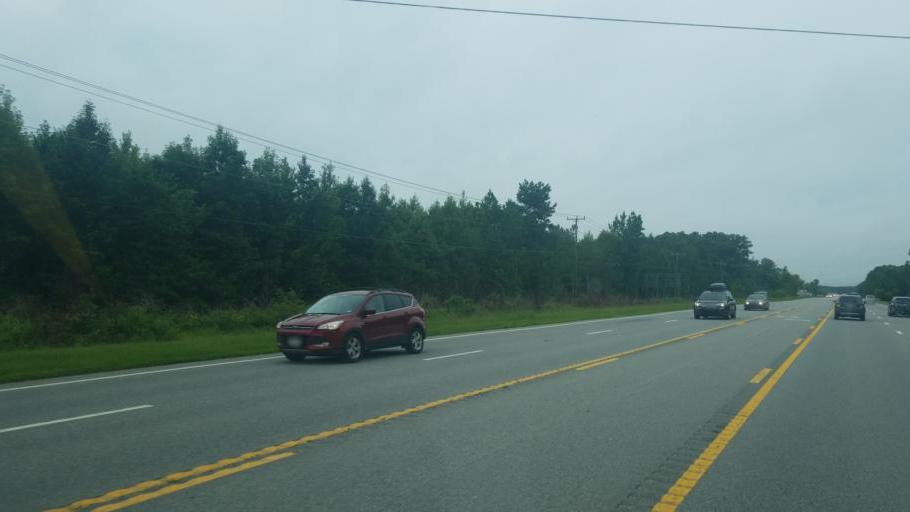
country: US
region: North Carolina
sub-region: Currituck County
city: Moyock
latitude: 36.4699
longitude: -76.1108
